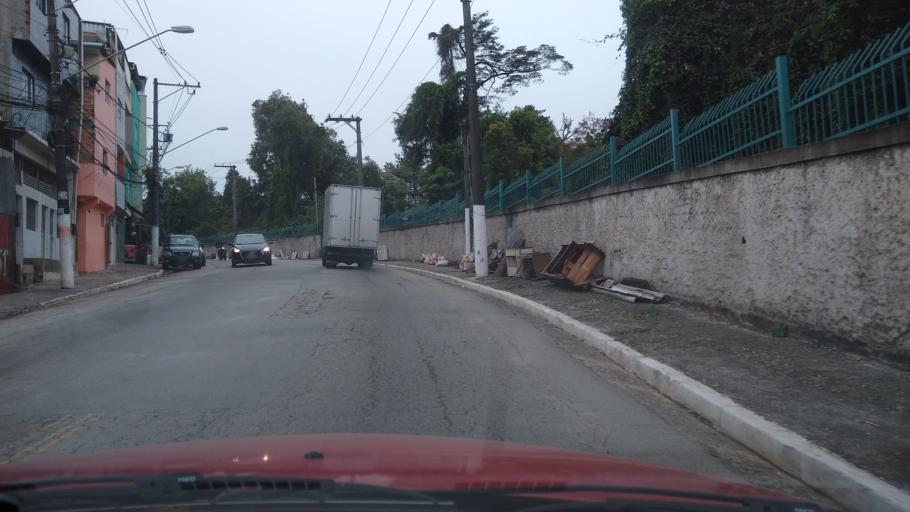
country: BR
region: Sao Paulo
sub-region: Diadema
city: Diadema
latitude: -23.6402
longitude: -46.6138
